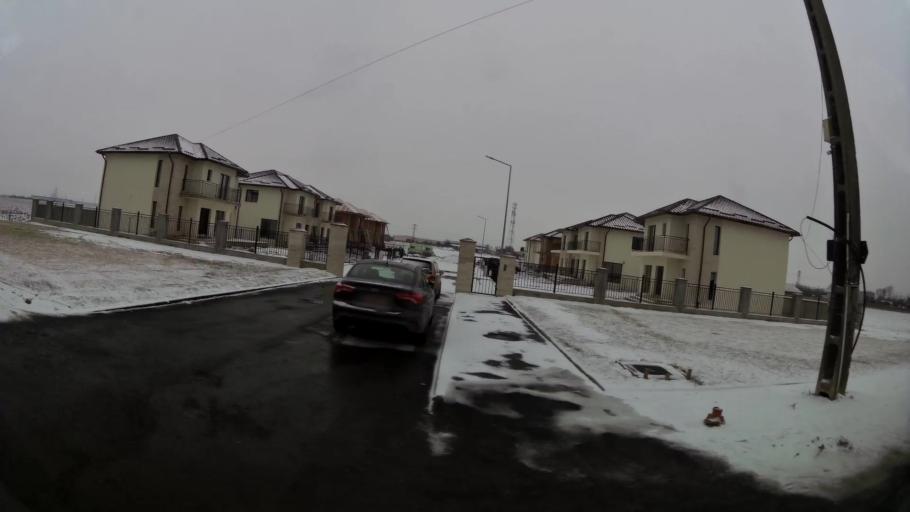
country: RO
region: Dambovita
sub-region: Comuna Ulmi
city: Ulmi
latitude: 44.8936
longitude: 25.5127
